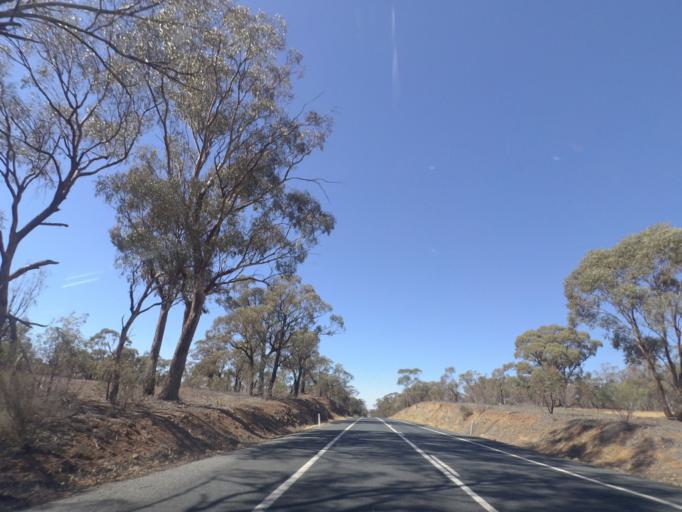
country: AU
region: New South Wales
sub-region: Bland
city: West Wyalong
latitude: -34.1663
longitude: 147.1159
